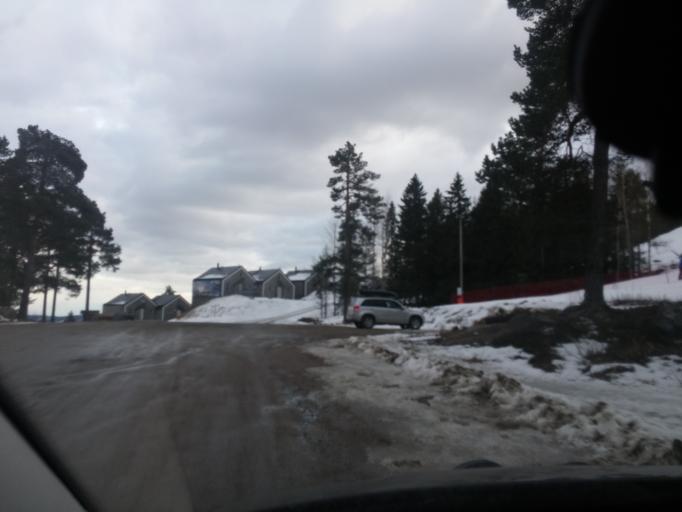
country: SE
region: Gaevleborg
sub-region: Ljusdals Kommun
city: Jaervsoe
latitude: 61.7190
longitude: 16.1577
